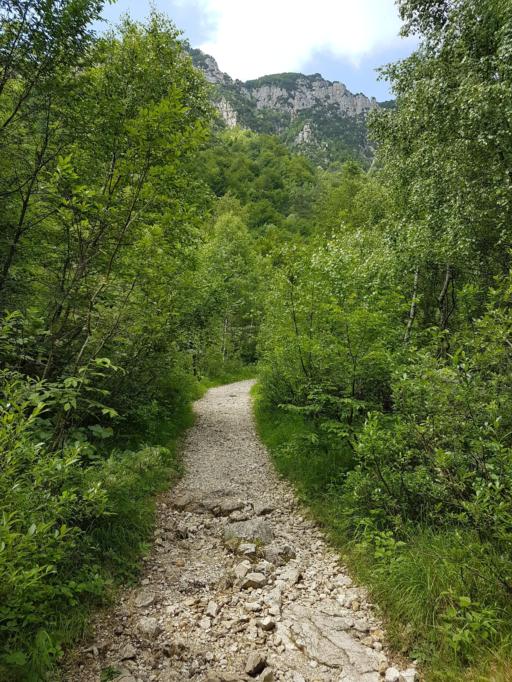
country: IT
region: Veneto
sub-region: Provincia di Vicenza
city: Recoaro Terme
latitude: 45.6776
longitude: 11.1998
